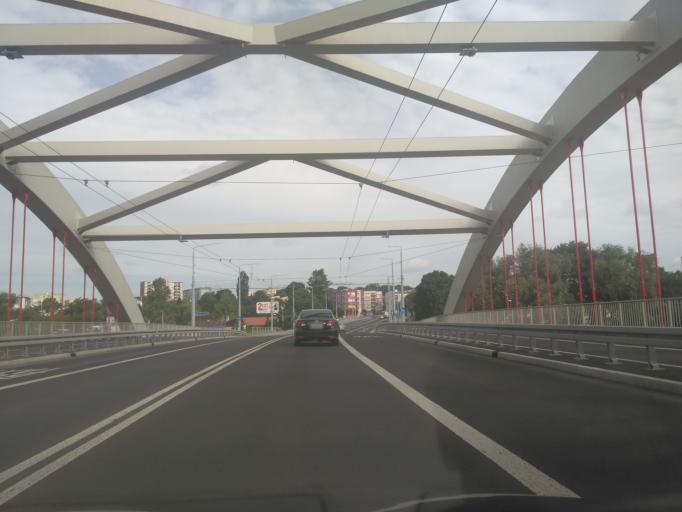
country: PL
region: Lublin Voivodeship
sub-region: Powiat lubelski
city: Lublin
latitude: 51.2350
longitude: 22.5572
